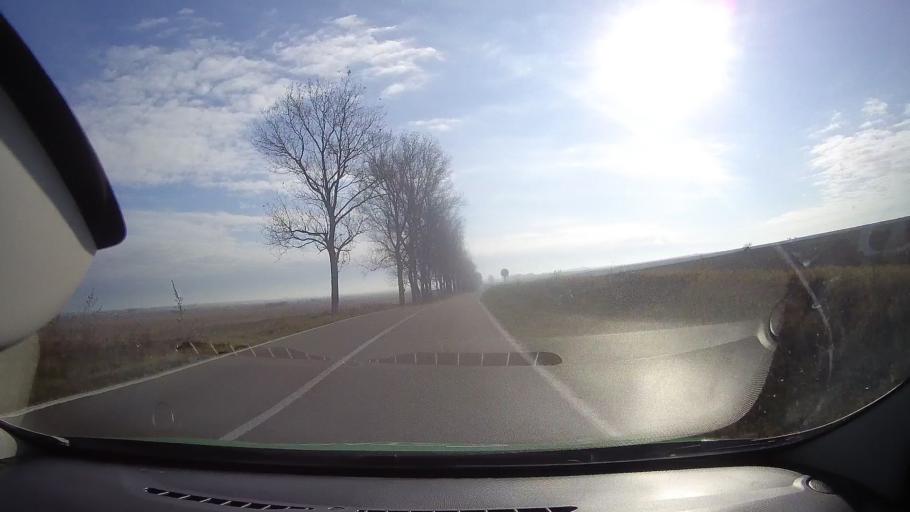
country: RO
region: Tulcea
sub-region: Comuna Mahmudia
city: Mahmudia
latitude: 45.0663
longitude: 29.1064
